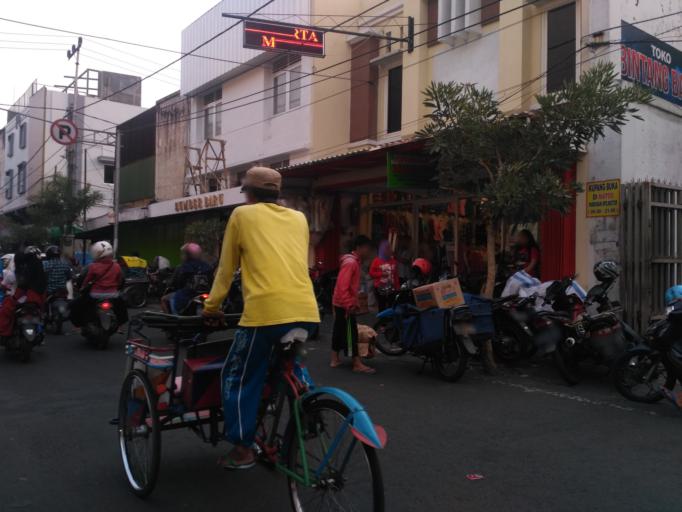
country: ID
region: East Java
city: Malang
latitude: -7.9865
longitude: 112.6329
